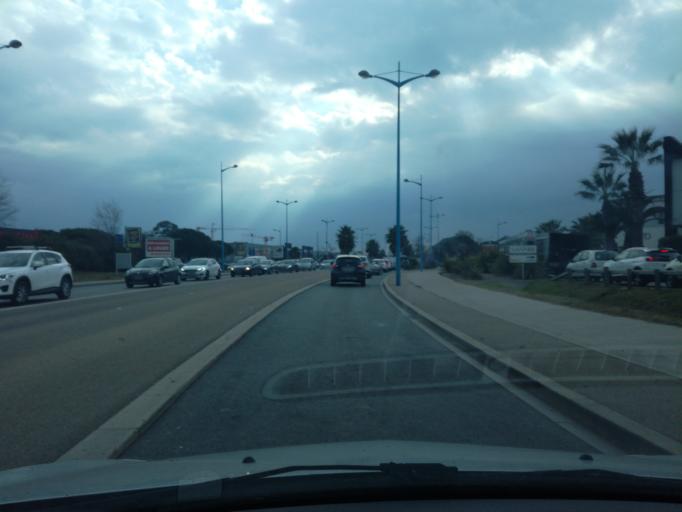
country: FR
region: Provence-Alpes-Cote d'Azur
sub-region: Departement des Alpes-Maritimes
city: Mandelieu-la-Napoule
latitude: 43.5558
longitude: 6.9538
